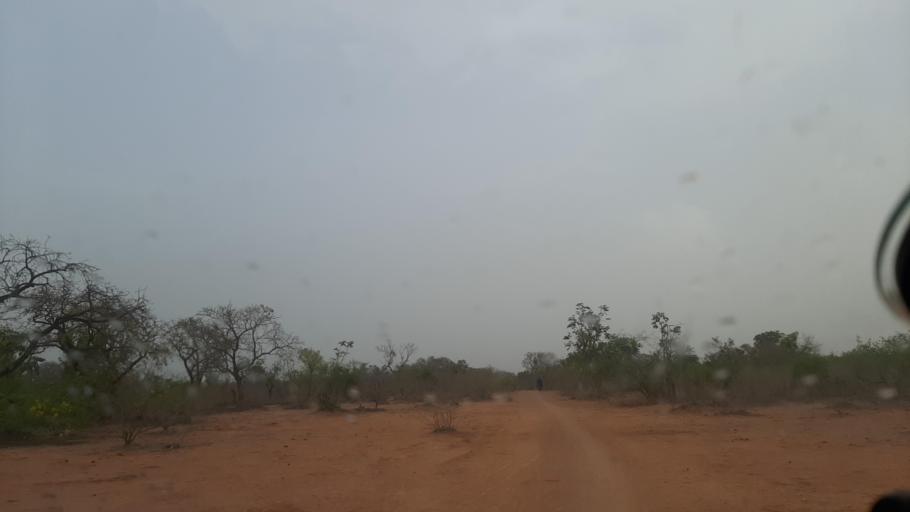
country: BF
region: Boucle du Mouhoun
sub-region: Province des Banwa
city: Salanso
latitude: 11.8646
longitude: -4.4412
